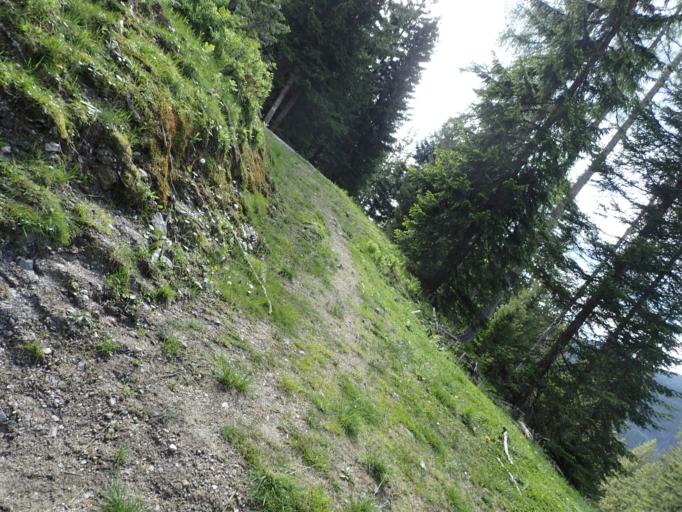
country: AT
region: Salzburg
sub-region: Politischer Bezirk Sankt Johann im Pongau
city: Kleinarl
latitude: 47.2318
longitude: 13.2784
